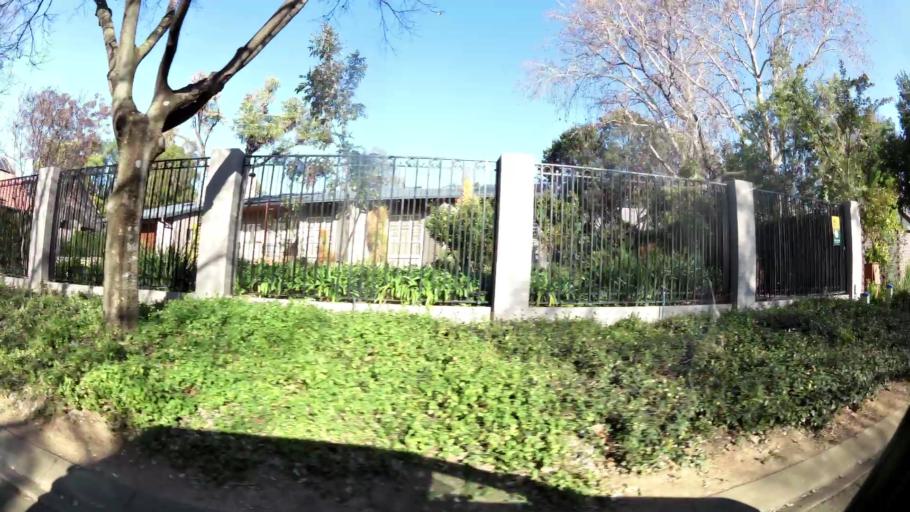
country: ZA
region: Gauteng
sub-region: City of Johannesburg Metropolitan Municipality
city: Roodepoort
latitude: -26.0864
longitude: 27.9516
